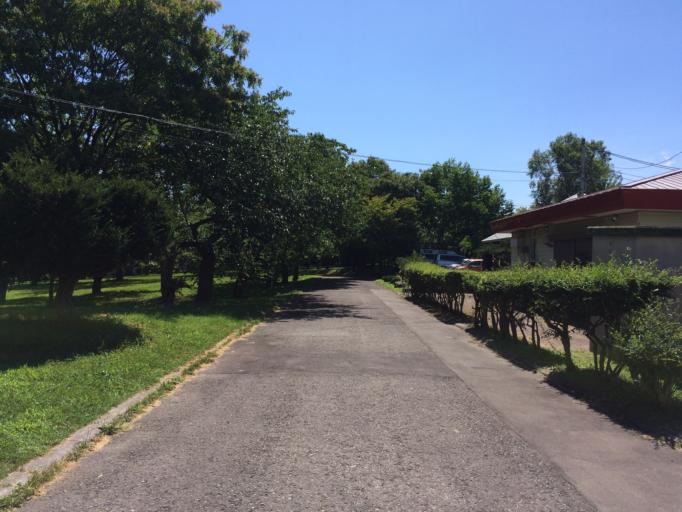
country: JP
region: Hokkaido
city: Nanae
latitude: 42.0994
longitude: 140.5681
